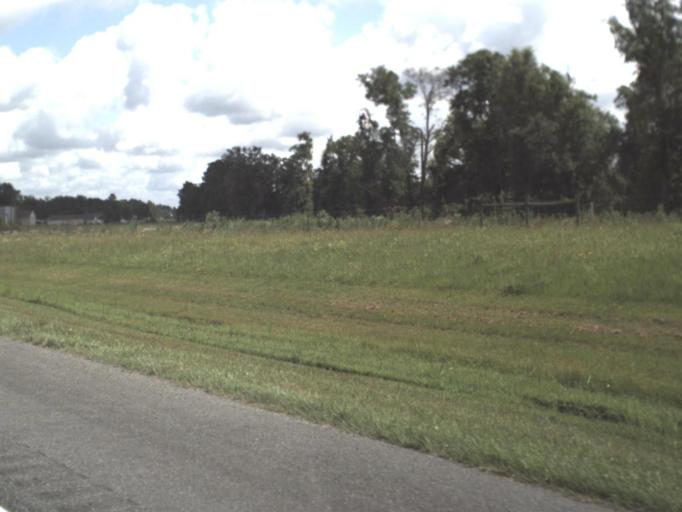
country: US
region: Florida
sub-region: Columbia County
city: Lake City
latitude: 30.1409
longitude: -82.6686
